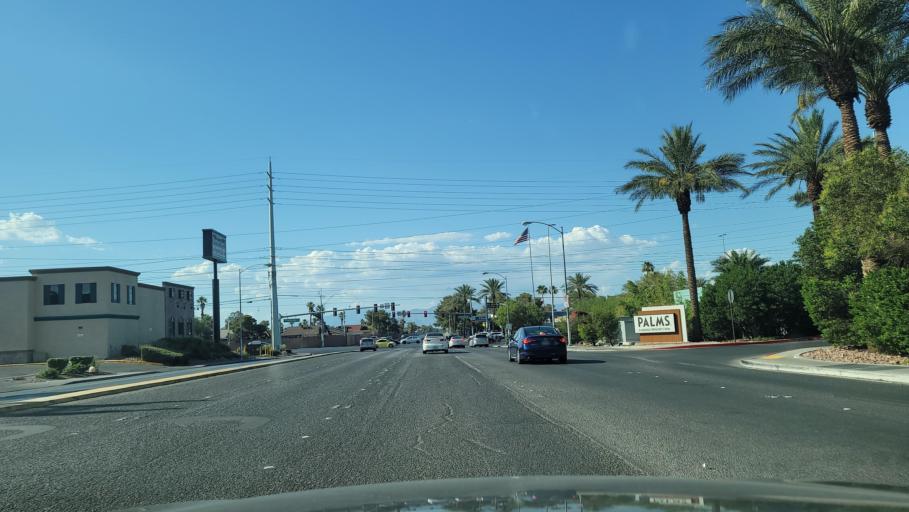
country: US
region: Nevada
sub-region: Clark County
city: Spring Valley
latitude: 36.1143
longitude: -115.1994
